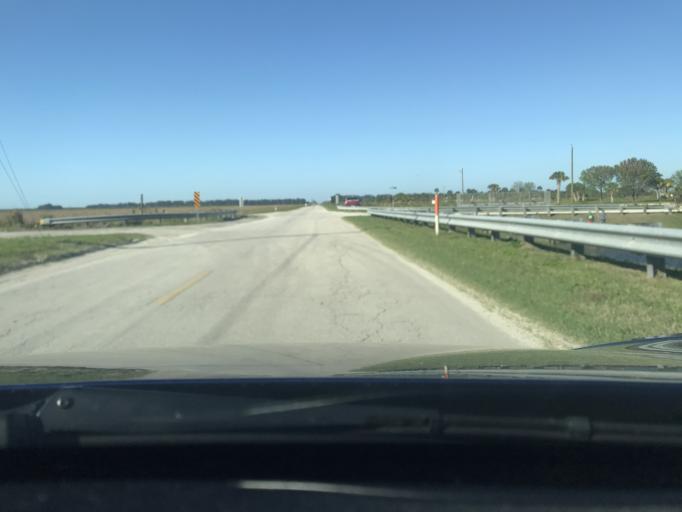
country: US
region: Florida
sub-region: Saint Lucie County
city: Lakewood Park
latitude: 27.4107
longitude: -80.4976
